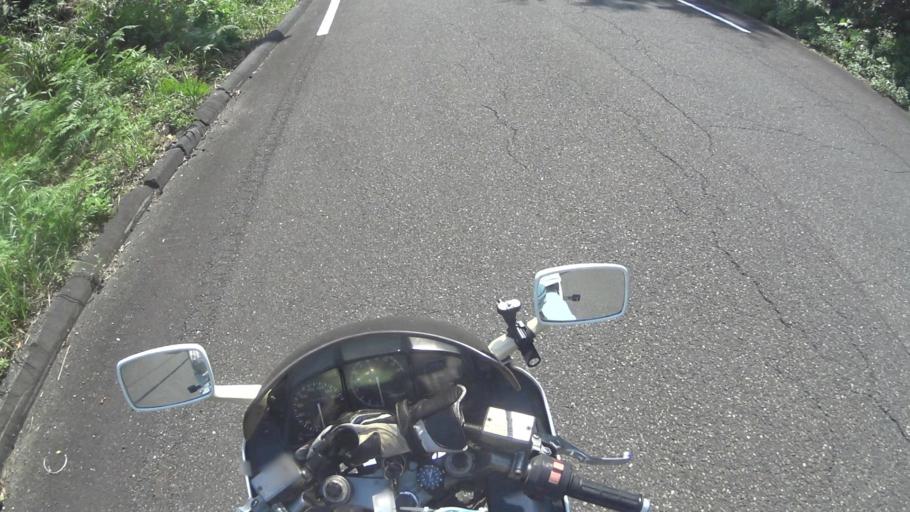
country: JP
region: Kyoto
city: Miyazu
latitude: 35.7056
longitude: 135.1917
